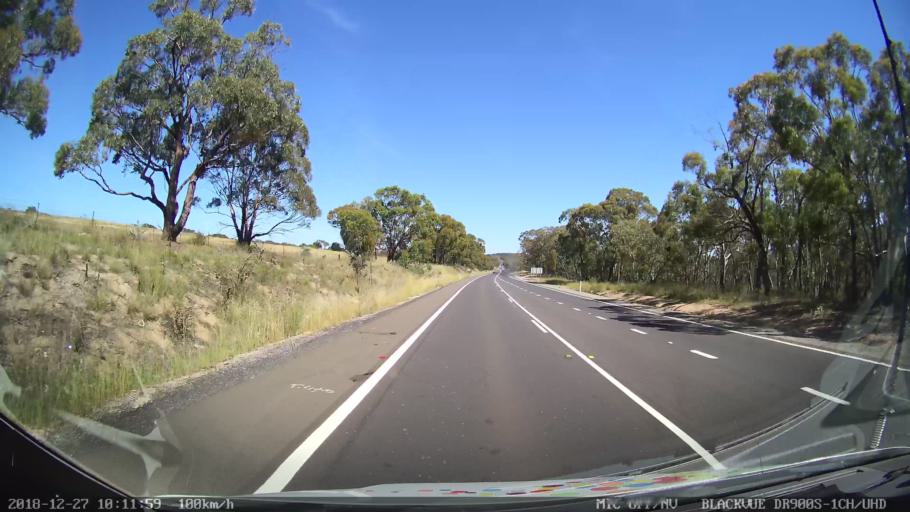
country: AU
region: New South Wales
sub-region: Bathurst Regional
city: Kelso
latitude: -33.4480
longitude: 149.7659
